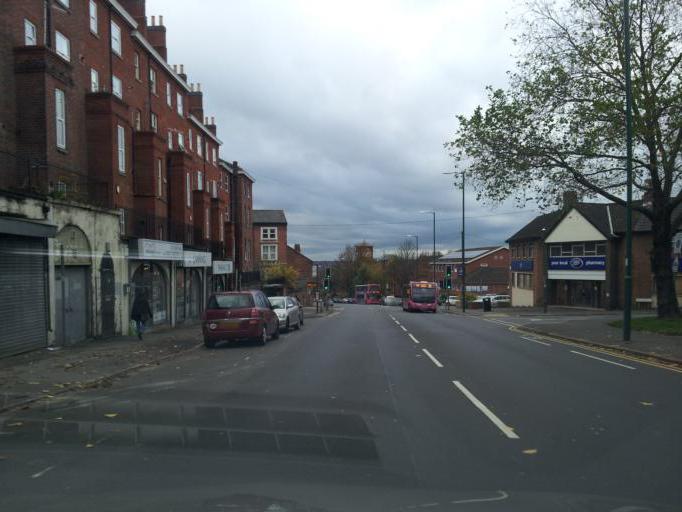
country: GB
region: England
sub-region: Nottingham
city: Nottingham
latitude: 52.9561
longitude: -1.1658
